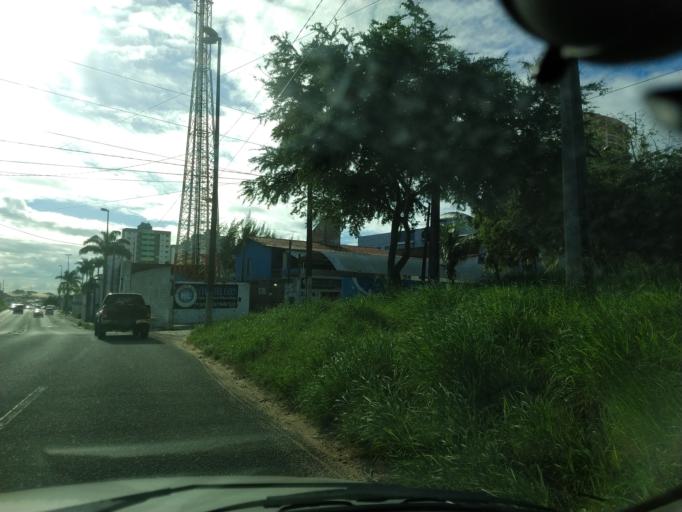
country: BR
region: Rio Grande do Norte
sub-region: Natal
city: Natal
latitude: -5.8392
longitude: -35.2238
